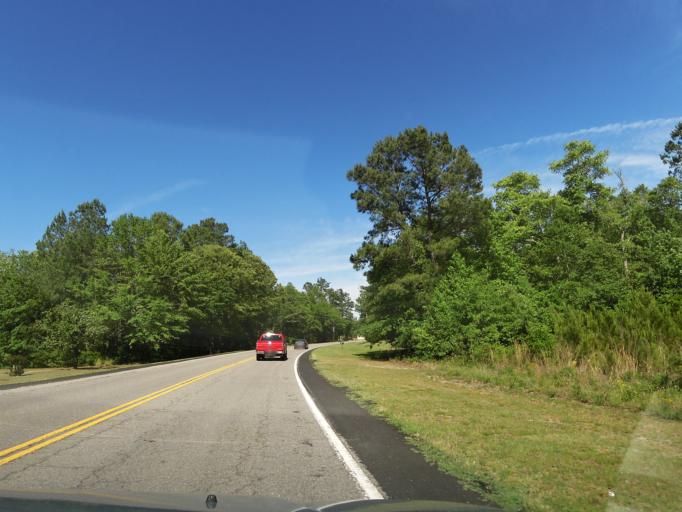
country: US
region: South Carolina
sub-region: Barnwell County
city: Blackville
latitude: 33.3490
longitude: -81.2308
